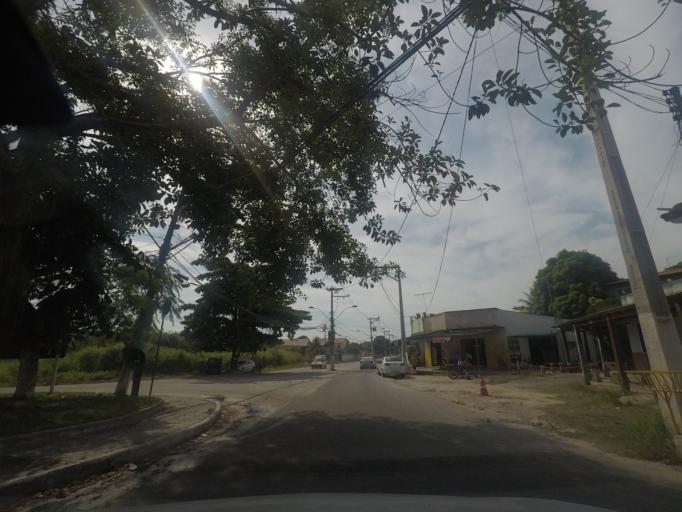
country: BR
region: Rio de Janeiro
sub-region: Marica
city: Marica
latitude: -22.9353
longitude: -42.9003
